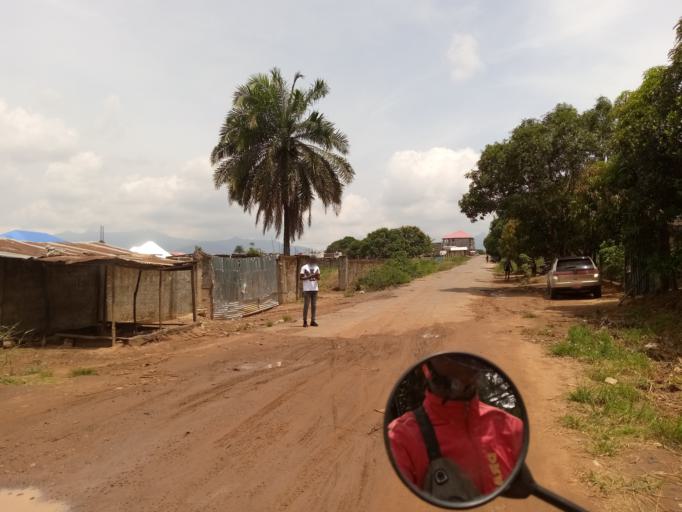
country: SL
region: Western Area
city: Waterloo
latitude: 8.3347
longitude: -13.0277
